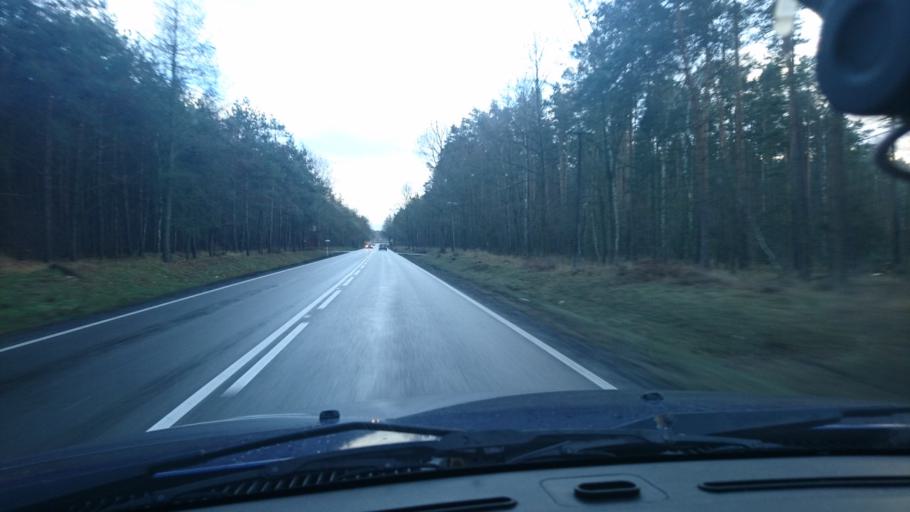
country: PL
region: Greater Poland Voivodeship
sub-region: Powiat kepinski
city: Kepno
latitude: 51.3374
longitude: 17.9538
